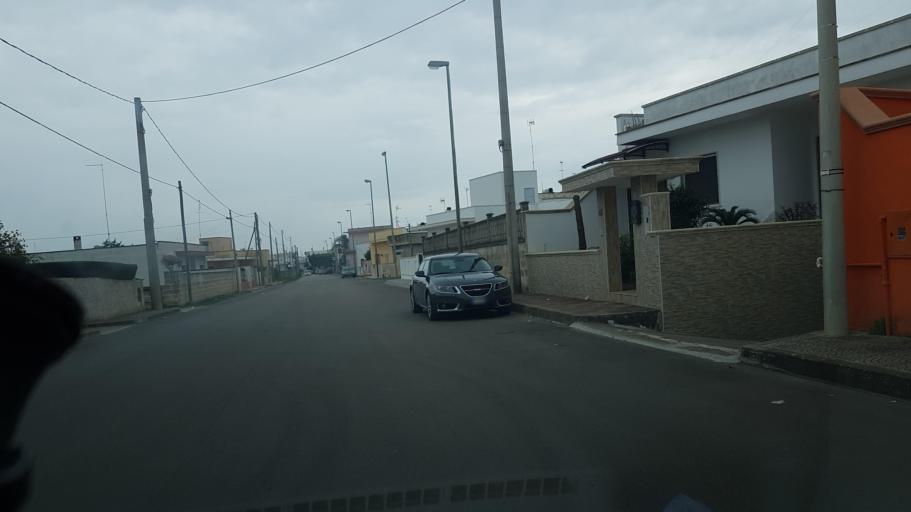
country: IT
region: Apulia
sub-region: Provincia di Lecce
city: Veglie
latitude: 40.3382
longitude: 17.9554
